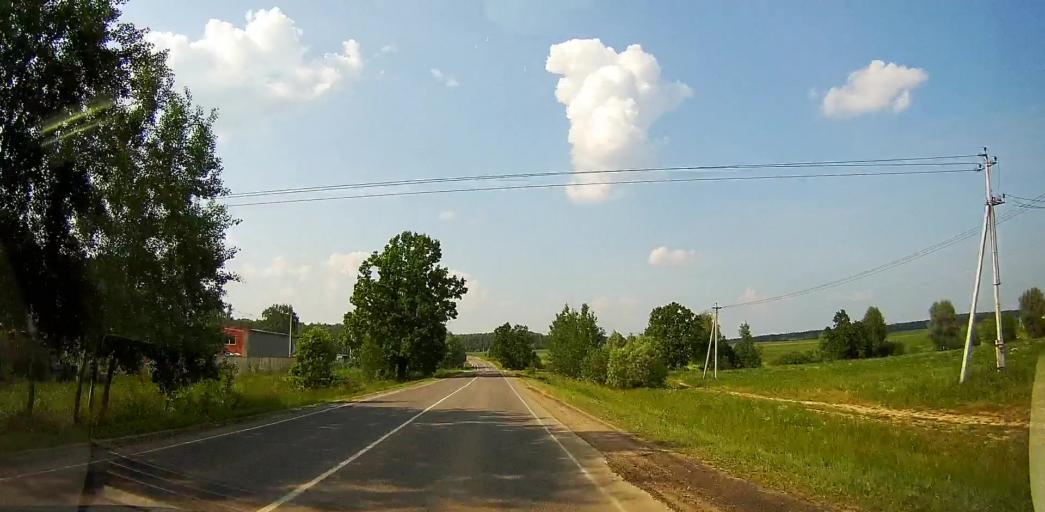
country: RU
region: Moskovskaya
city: Il'inskoye
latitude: 55.2034
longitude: 37.9630
